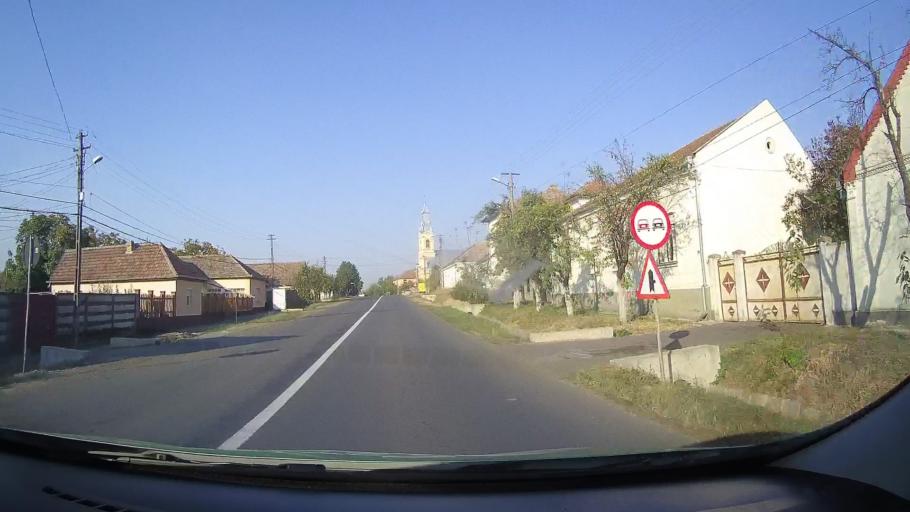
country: RO
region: Arad
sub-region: Comuna Ghioroc
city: Cuvin
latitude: 46.1651
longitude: 21.5930
